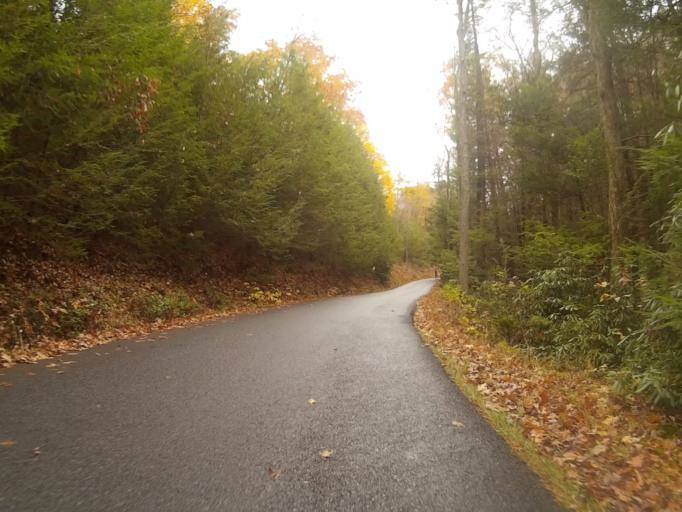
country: US
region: Pennsylvania
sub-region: Centre County
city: Boalsburg
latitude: 40.7633
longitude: -77.7355
